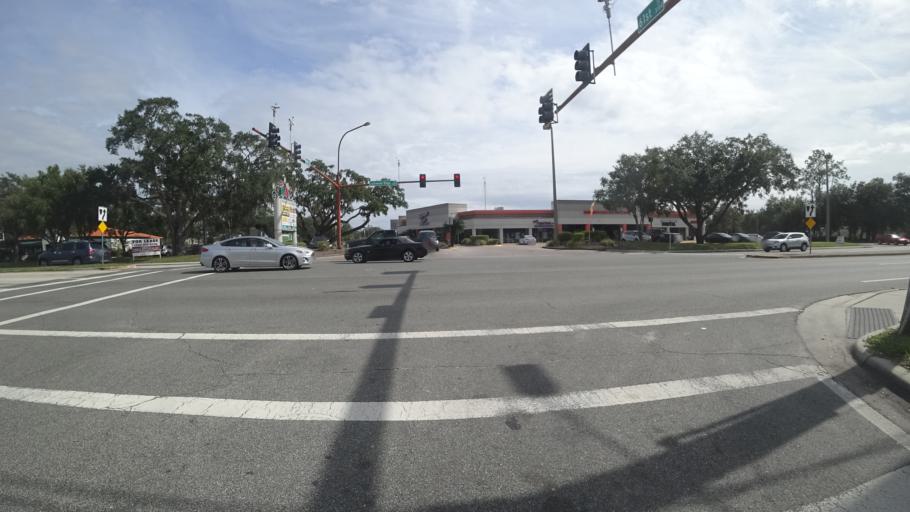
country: US
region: Florida
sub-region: Sarasota County
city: North Sarasota
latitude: 27.3869
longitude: -82.5058
